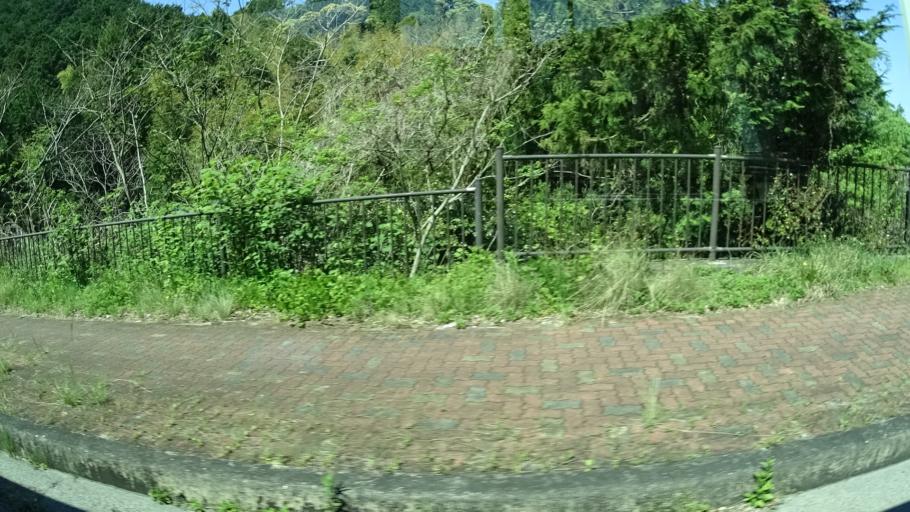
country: JP
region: Mie
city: Toba
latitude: 34.5025
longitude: 136.7813
